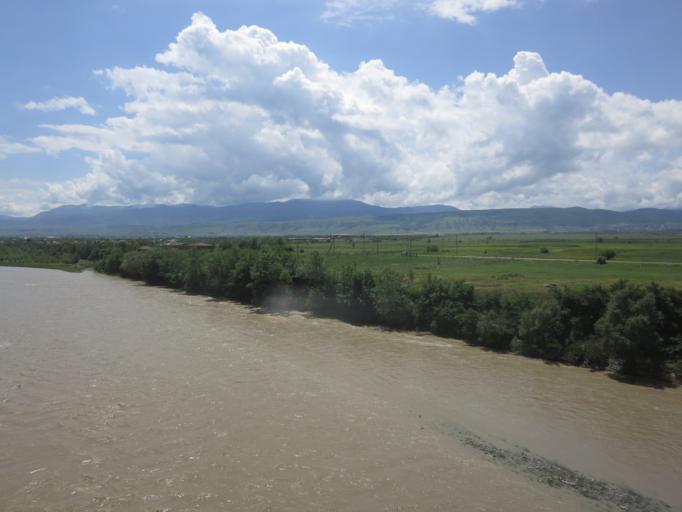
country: GE
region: Shida Kartli
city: Kaspi
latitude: 41.9476
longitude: 44.2829
